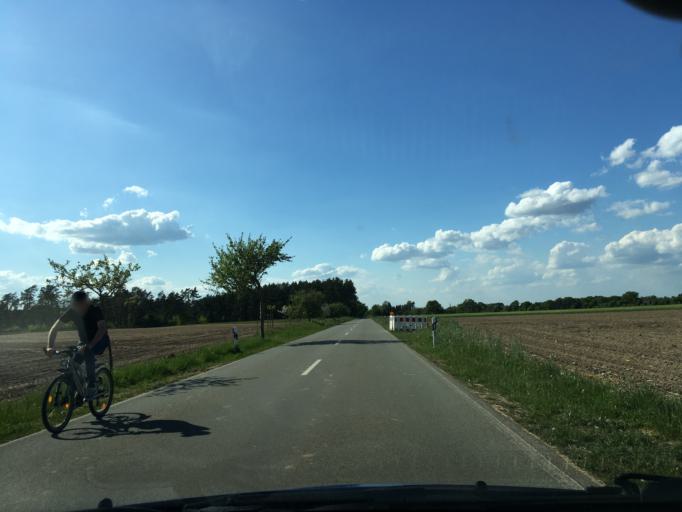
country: DE
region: Lower Saxony
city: Gartow
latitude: 53.0612
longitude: 11.4193
